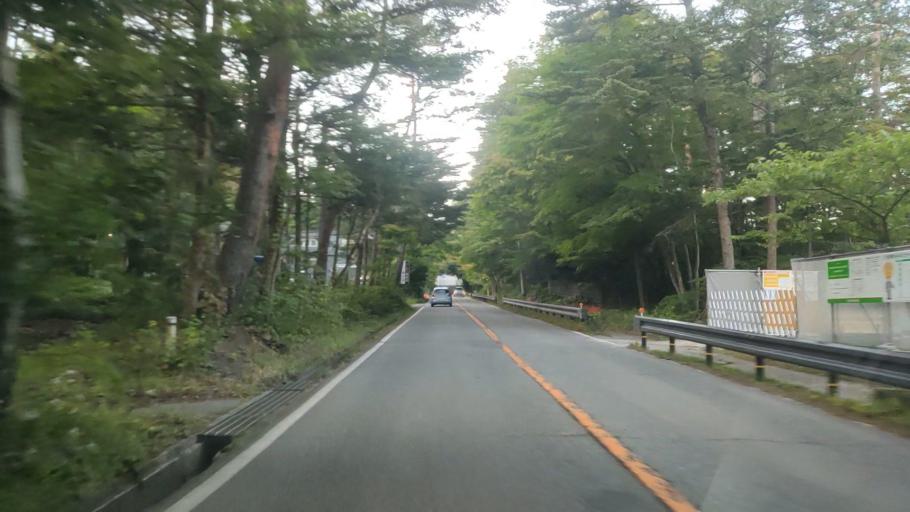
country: JP
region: Nagano
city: Komoro
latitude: 36.3700
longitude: 138.5876
